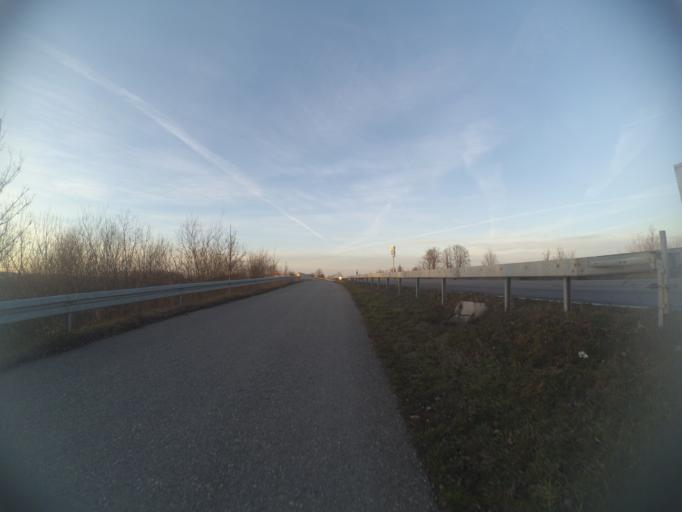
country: DE
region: Bavaria
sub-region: Swabia
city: Wasserburg
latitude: 48.4308
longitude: 10.2920
